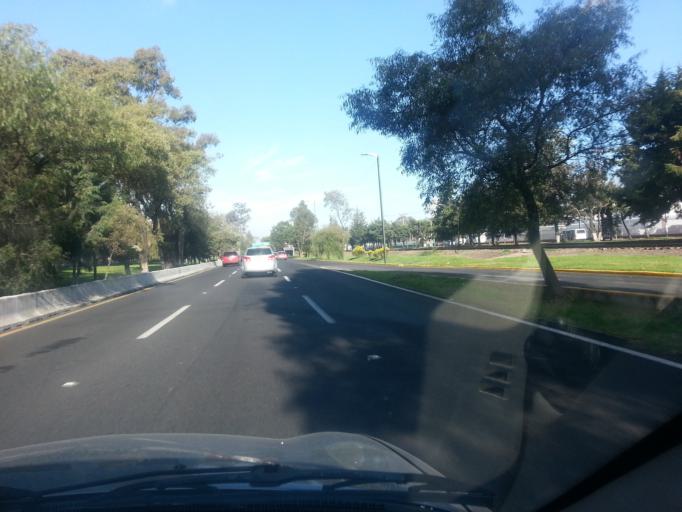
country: MX
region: Mexico
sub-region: Lerma
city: Colonia Isidro Fabela
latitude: 19.2858
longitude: -99.5324
